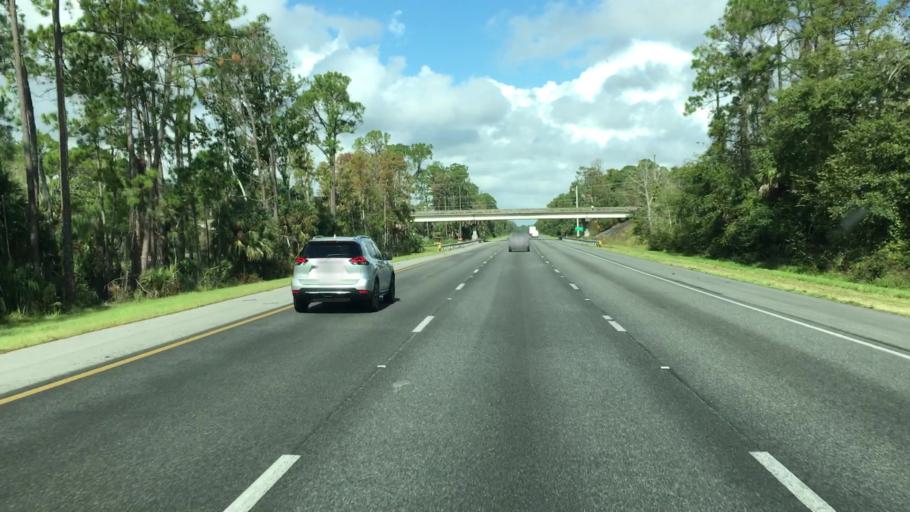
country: US
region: Florida
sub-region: Volusia County
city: Glencoe
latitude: 29.0458
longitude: -81.0066
